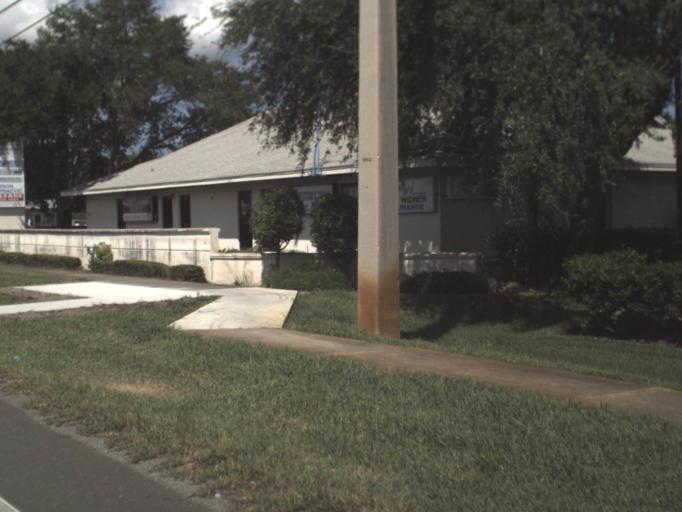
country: US
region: Florida
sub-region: Manatee County
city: West Bradenton
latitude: 27.4961
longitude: -82.6238
